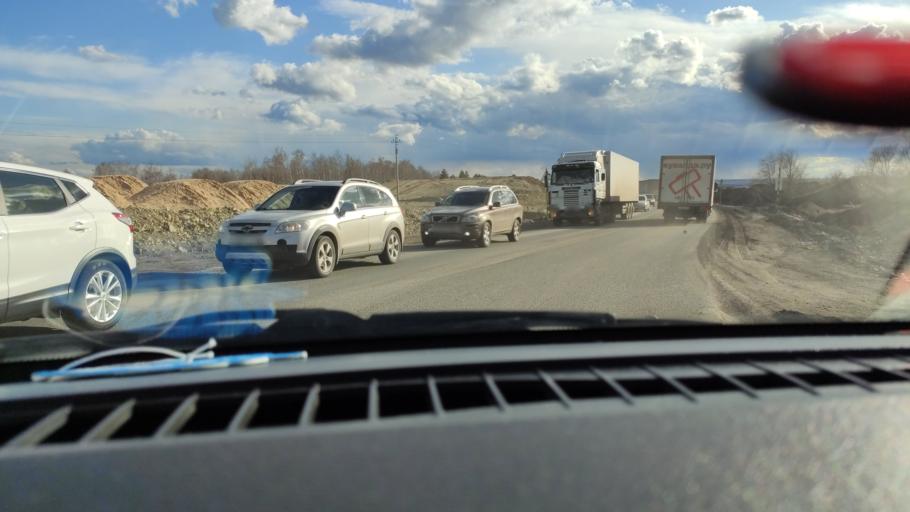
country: RU
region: Saratov
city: Sinodskoye
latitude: 52.0082
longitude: 46.6856
